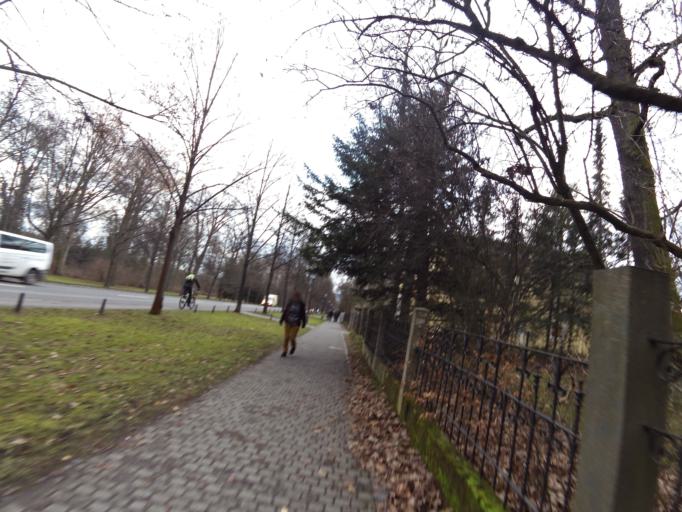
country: DE
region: Thuringia
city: Weimar
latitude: 50.9704
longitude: 11.3340
